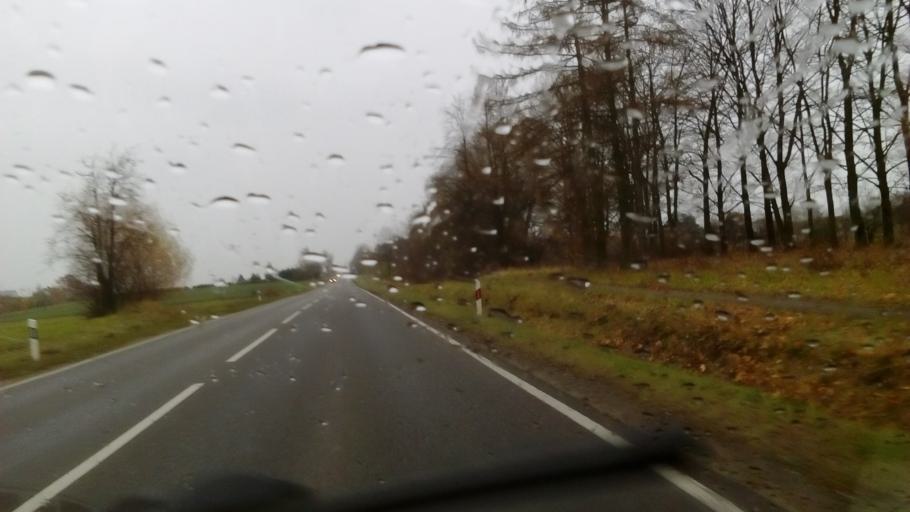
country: LT
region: Marijampoles apskritis
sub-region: Marijampole Municipality
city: Marijampole
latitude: 54.5487
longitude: 23.4129
